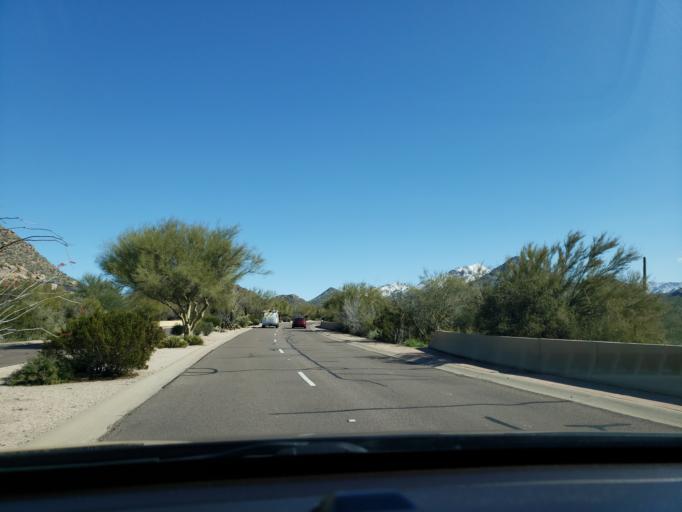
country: US
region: Arizona
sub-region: Maricopa County
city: Carefree
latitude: 33.7123
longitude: -111.8547
